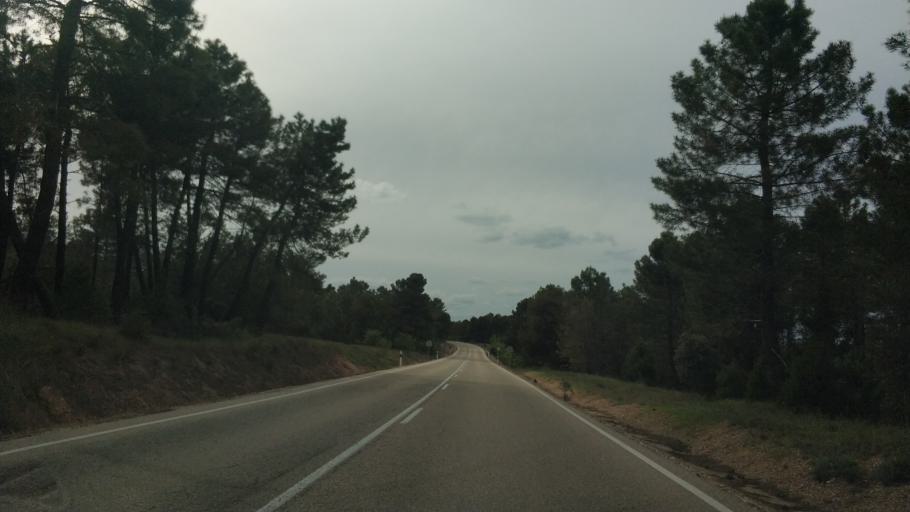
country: ES
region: Castille and Leon
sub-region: Provincia de Soria
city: Valdenebro
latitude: 41.5563
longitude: -2.9662
